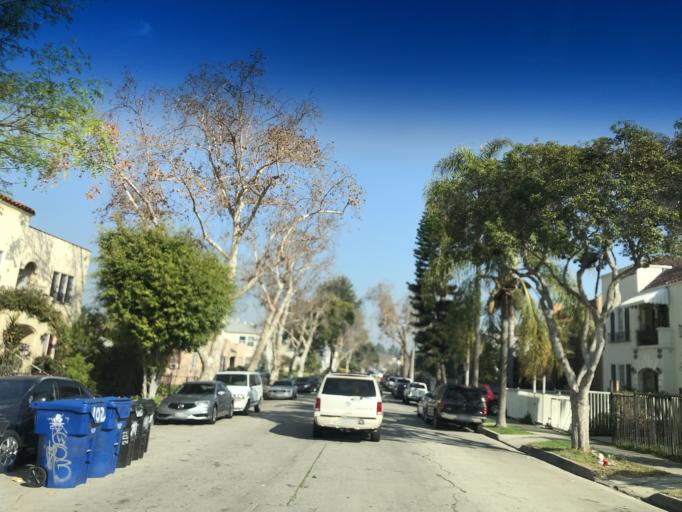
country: US
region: California
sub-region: Los Angeles County
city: Hollywood
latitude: 34.0500
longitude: -118.3298
